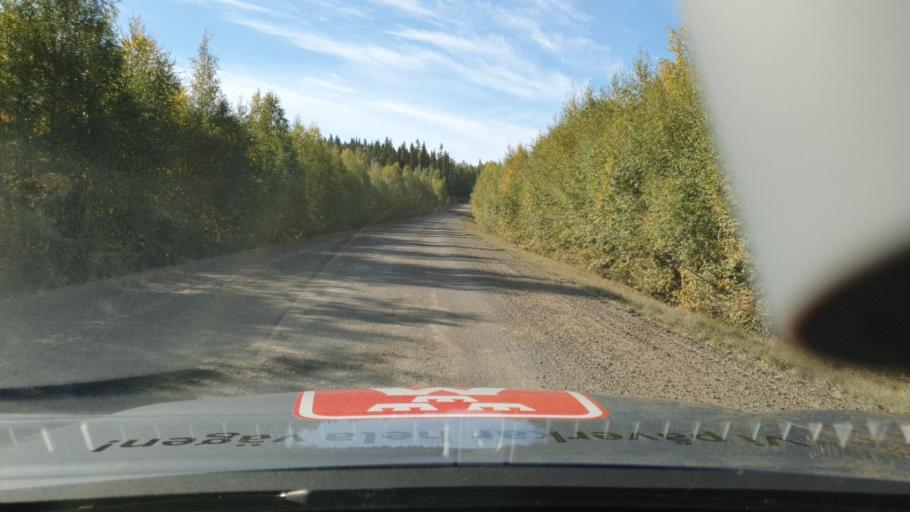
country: SE
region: Norrbotten
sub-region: Alvsbyns Kommun
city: AElvsbyn
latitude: 66.0856
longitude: 20.8186
